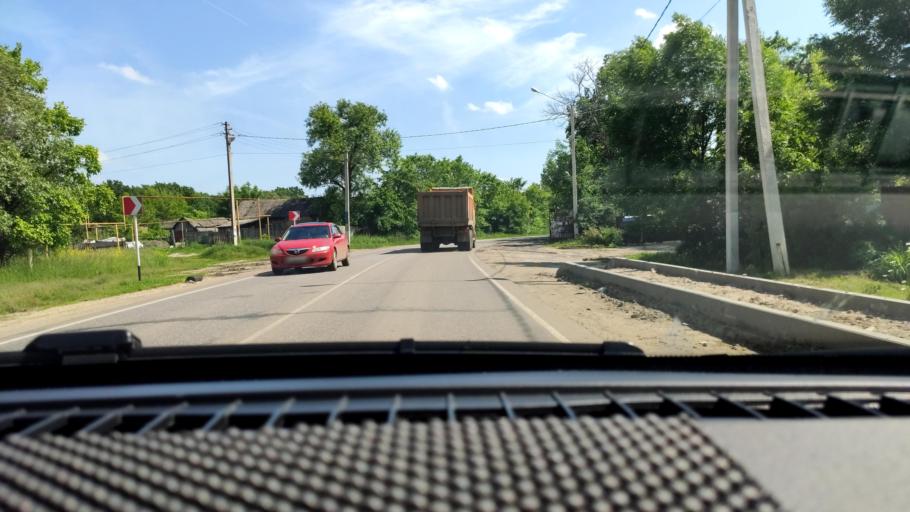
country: RU
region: Voronezj
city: Semiluki
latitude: 51.7599
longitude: 39.0401
